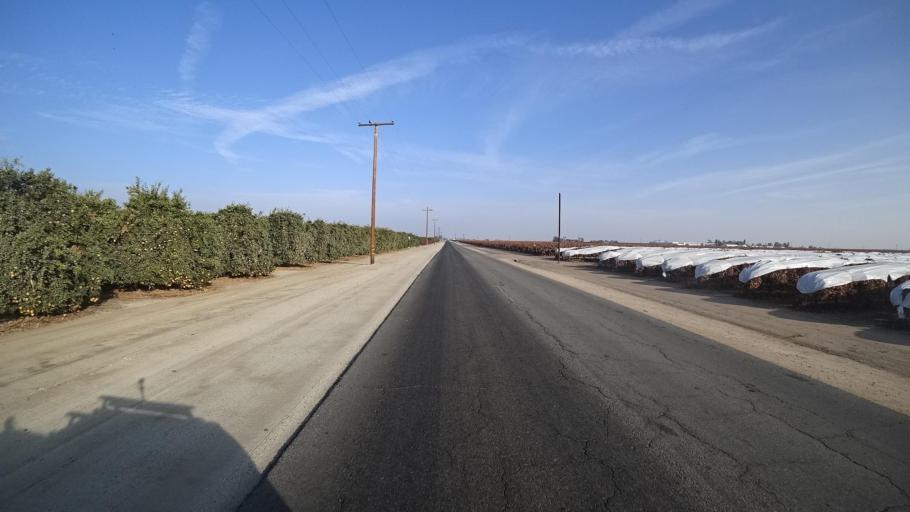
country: US
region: California
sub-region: Kern County
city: Delano
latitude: 35.7646
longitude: -119.1875
